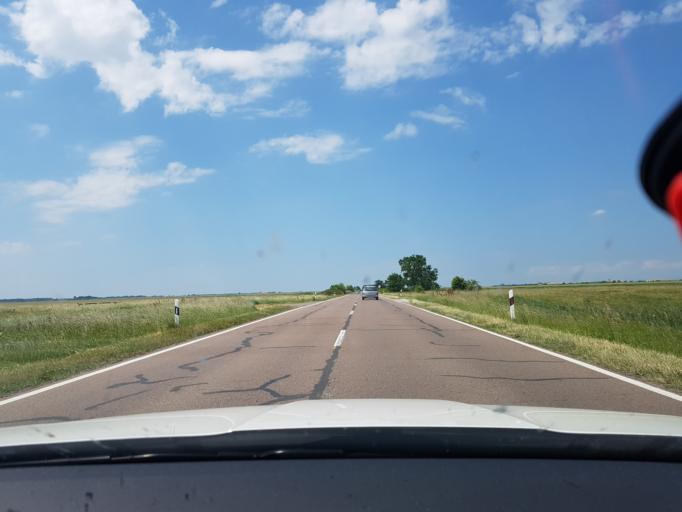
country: HU
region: Hajdu-Bihar
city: Hortobagy
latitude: 47.5826
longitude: 21.1347
